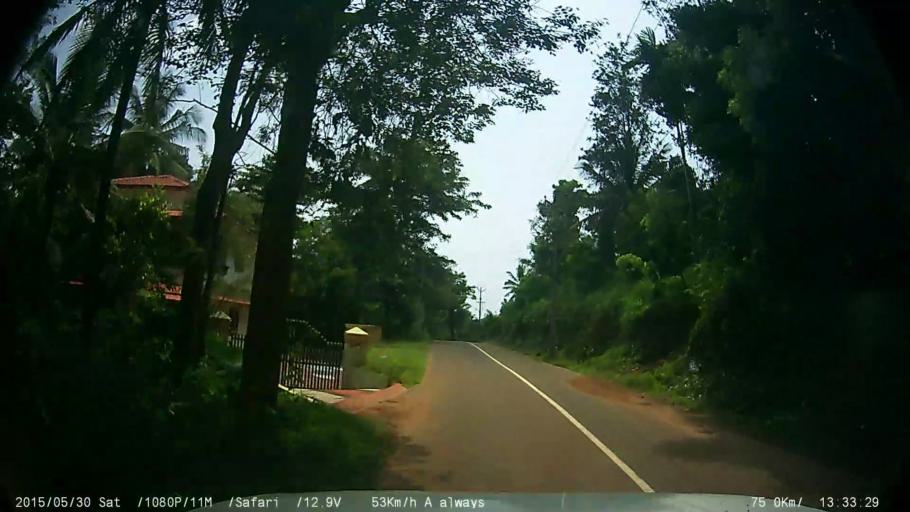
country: IN
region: Kerala
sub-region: Wayanad
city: Panamaram
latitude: 11.8203
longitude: 76.0718
